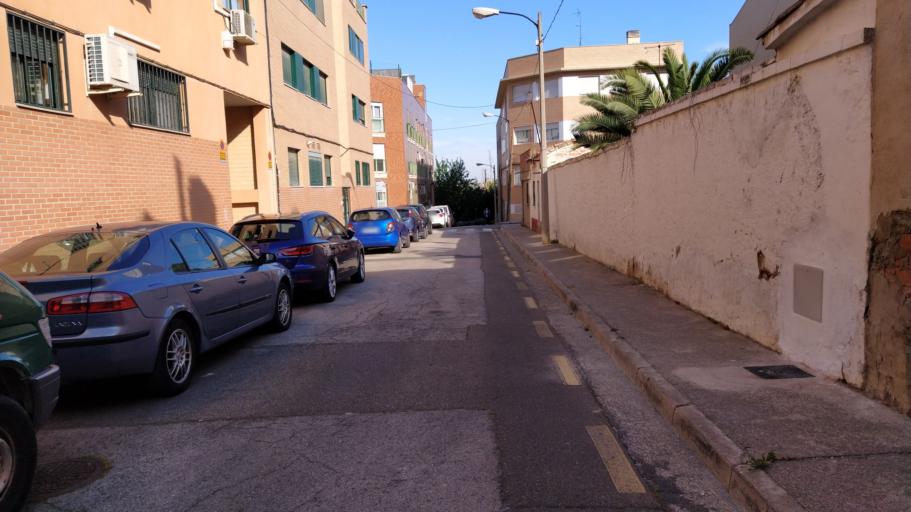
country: ES
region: Aragon
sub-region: Provincia de Zaragoza
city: Oliver-Valdefierro, Oliver, Valdefierro
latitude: 41.6389
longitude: -0.9359
